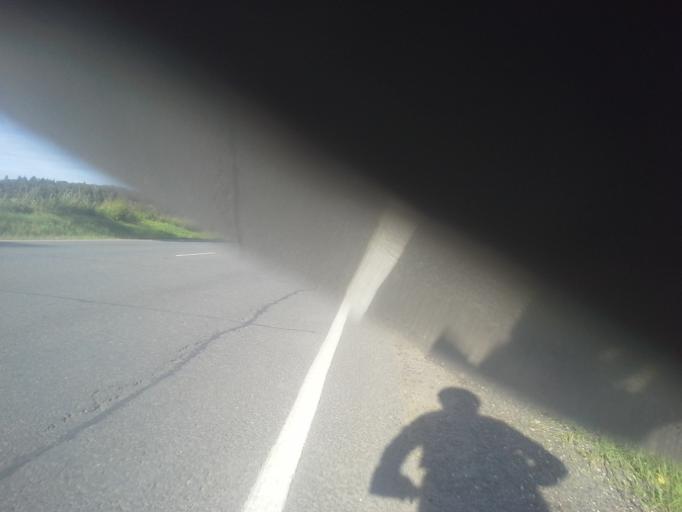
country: RU
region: Moskovskaya
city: Nazar'yevo
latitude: 55.6746
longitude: 37.0510
